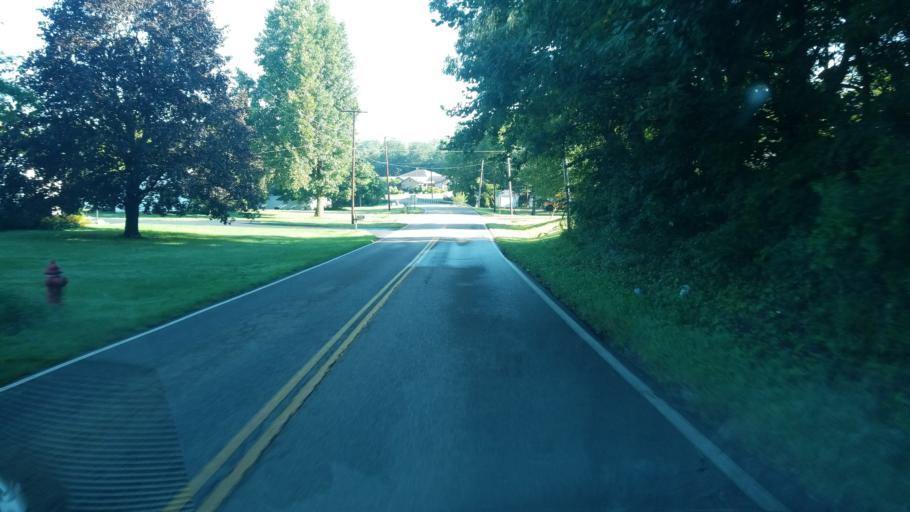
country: US
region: Ohio
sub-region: Knox County
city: Mount Vernon
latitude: 40.4148
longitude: -82.4950
